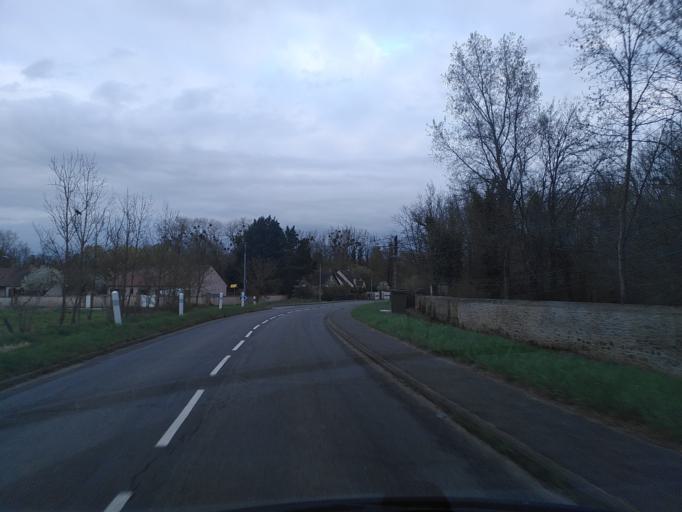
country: FR
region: Ile-de-France
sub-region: Departement de l'Essonne
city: Bruyeres-le-Chatel
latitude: 48.5831
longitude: 2.1931
